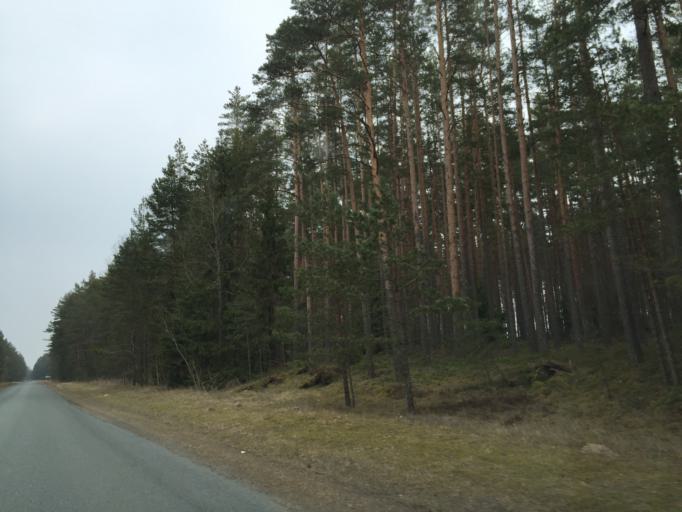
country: LV
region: Salacgrivas
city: Ainazi
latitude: 57.9881
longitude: 24.4235
